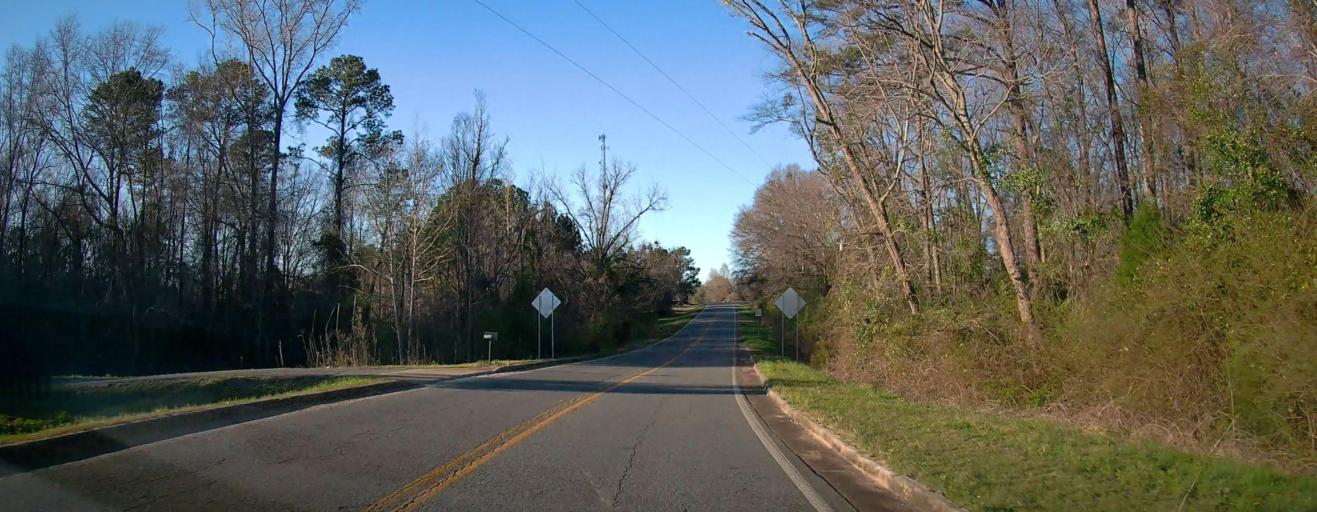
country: US
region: Georgia
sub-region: Talbot County
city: Talbotton
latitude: 32.5801
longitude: -84.5530
